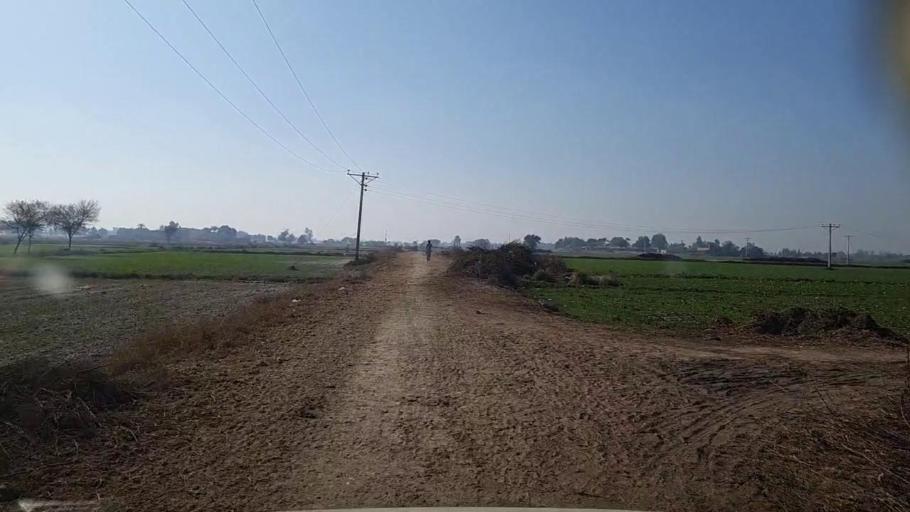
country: PK
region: Sindh
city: Khairpur
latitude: 27.9312
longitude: 69.6953
